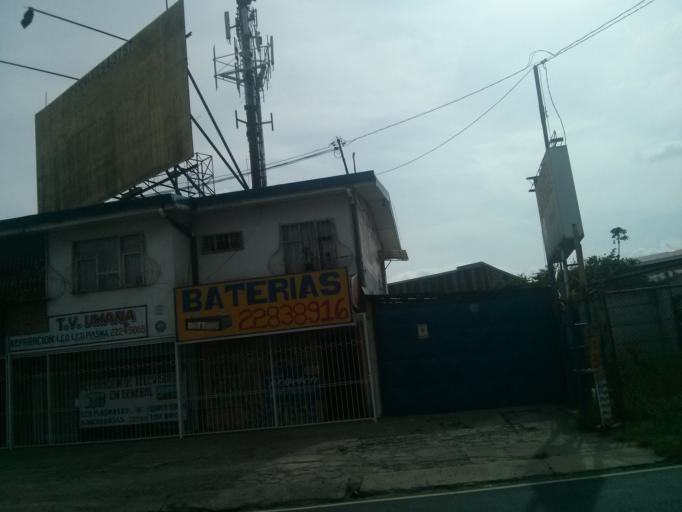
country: CR
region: San Jose
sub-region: Canton de Goicoechea
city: Guadalupe
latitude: 9.9424
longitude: -84.0602
